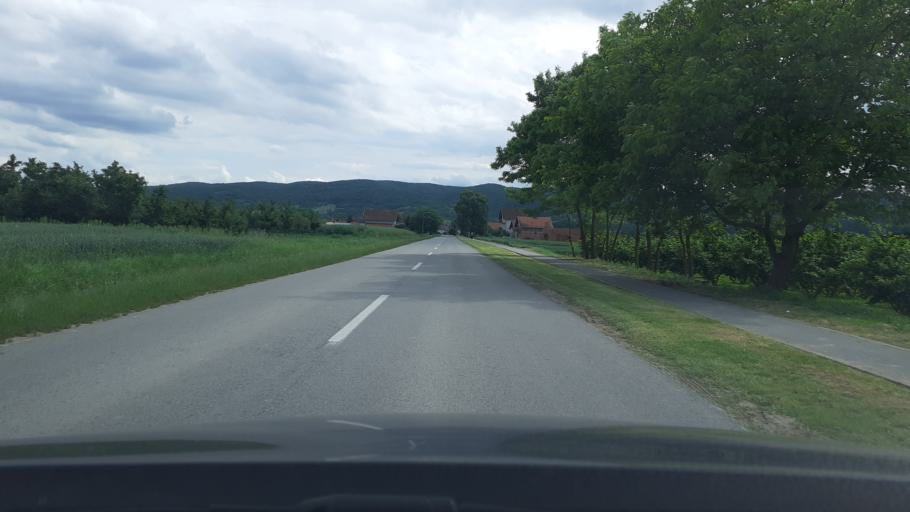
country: HR
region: Pozesko-Slavonska
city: Jaksic
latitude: 45.3456
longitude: 17.7566
